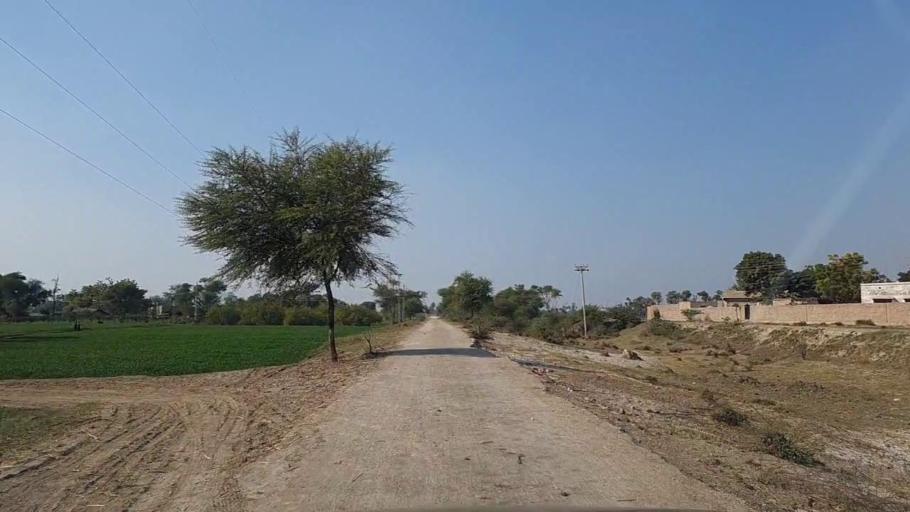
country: PK
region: Sindh
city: Daur
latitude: 26.3815
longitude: 68.3296
